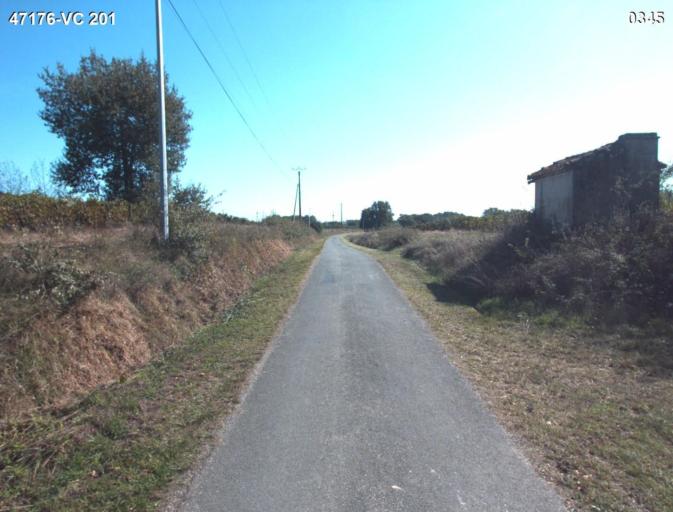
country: FR
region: Aquitaine
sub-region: Departement du Lot-et-Garonne
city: Vianne
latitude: 44.2109
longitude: 0.3099
